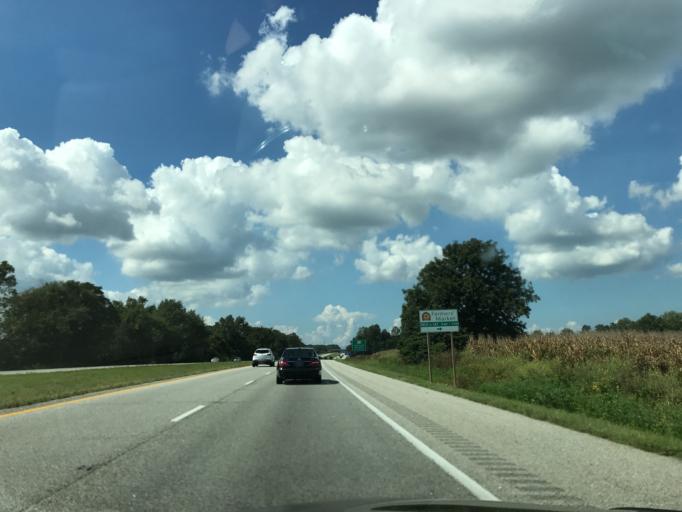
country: US
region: Maryland
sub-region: Queen Anne's County
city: Centreville
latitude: 39.0162
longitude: -76.0606
